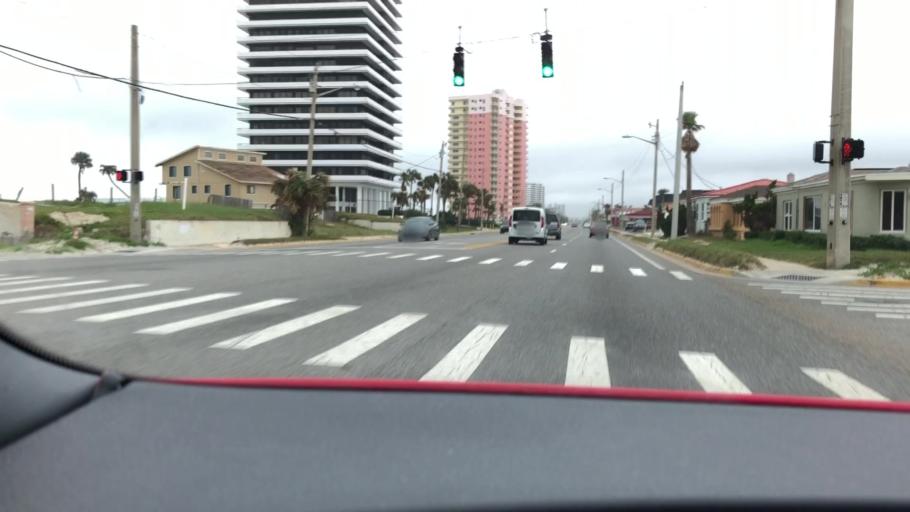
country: US
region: Florida
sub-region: Volusia County
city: Holly Hill
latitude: 29.2592
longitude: -81.0237
